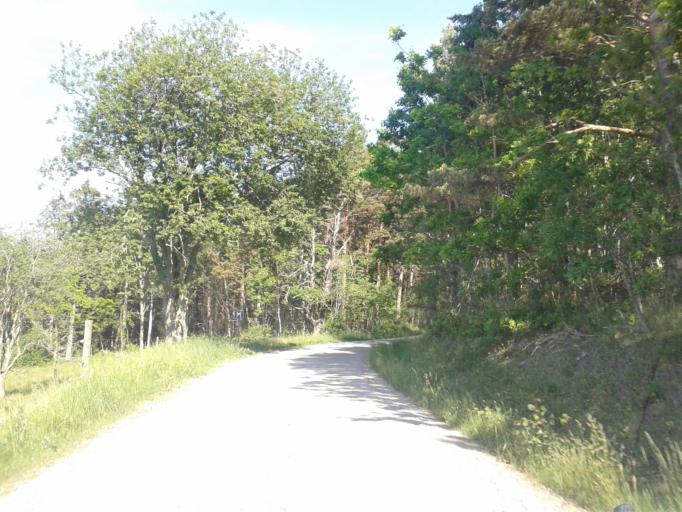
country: SE
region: Vaestra Goetaland
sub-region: Stromstads Kommun
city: Stroemstad
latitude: 58.8588
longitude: 11.2295
